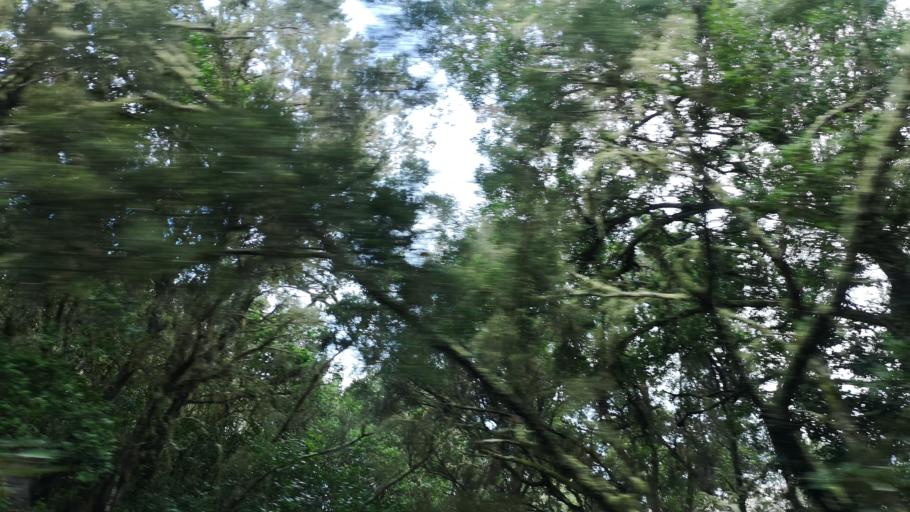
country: ES
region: Canary Islands
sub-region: Provincia de Santa Cruz de Tenerife
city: Vallehermosa
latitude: 28.1619
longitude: -17.2969
